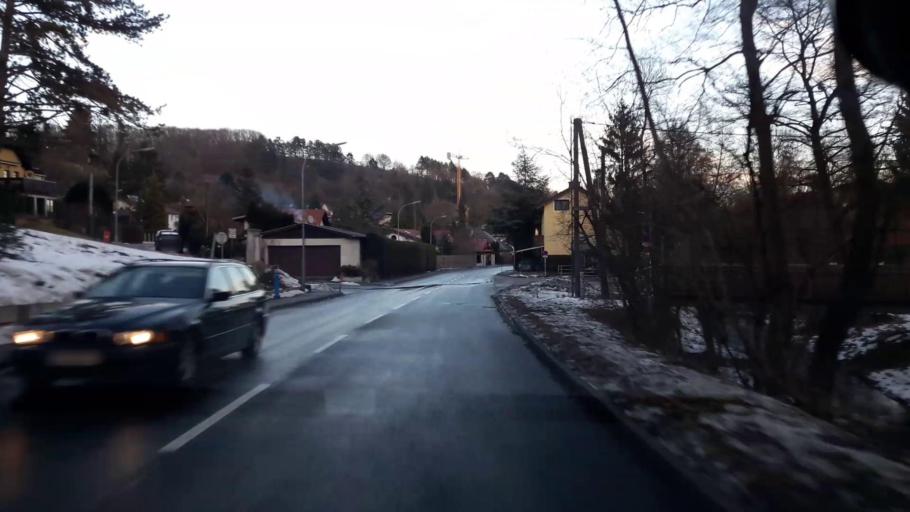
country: AT
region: Lower Austria
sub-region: Politischer Bezirk Wien-Umgebung
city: Klosterneuburg
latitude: 48.2856
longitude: 16.2930
